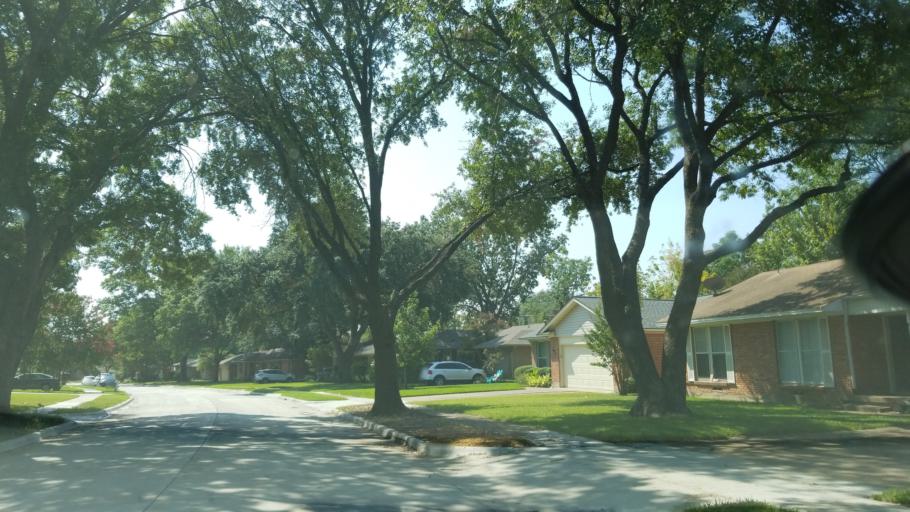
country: US
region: Texas
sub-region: Dallas County
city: Richardson
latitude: 32.8740
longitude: -96.7064
